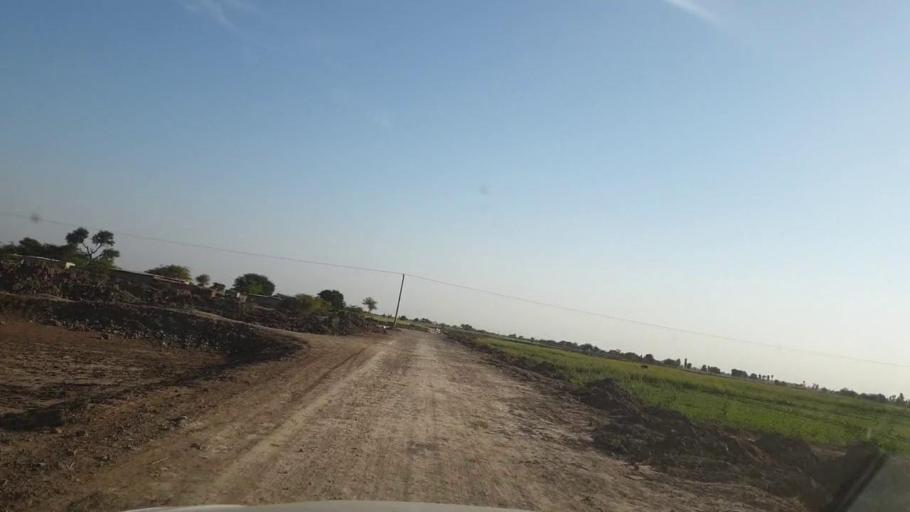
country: PK
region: Sindh
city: Kunri
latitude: 25.0899
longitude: 69.4234
